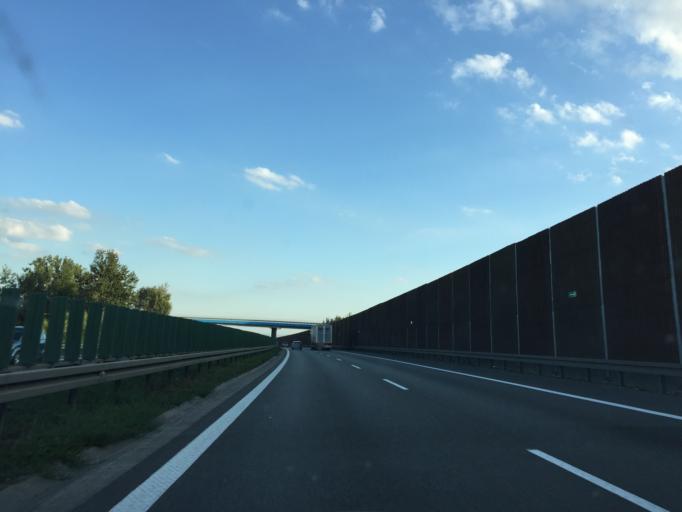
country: PL
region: Lesser Poland Voivodeship
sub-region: Powiat krakowski
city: Kryspinow
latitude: 50.0632
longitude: 19.8096
